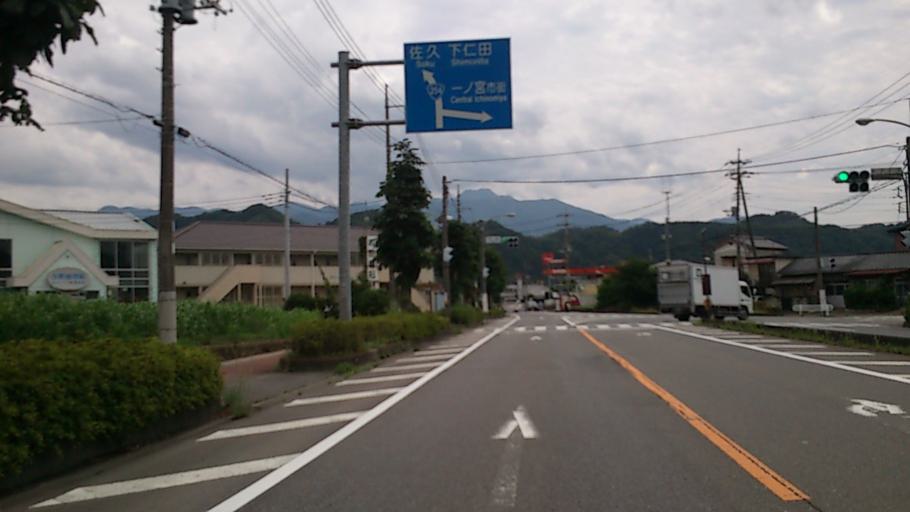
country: JP
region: Gunma
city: Tomioka
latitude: 36.2480
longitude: 138.8595
